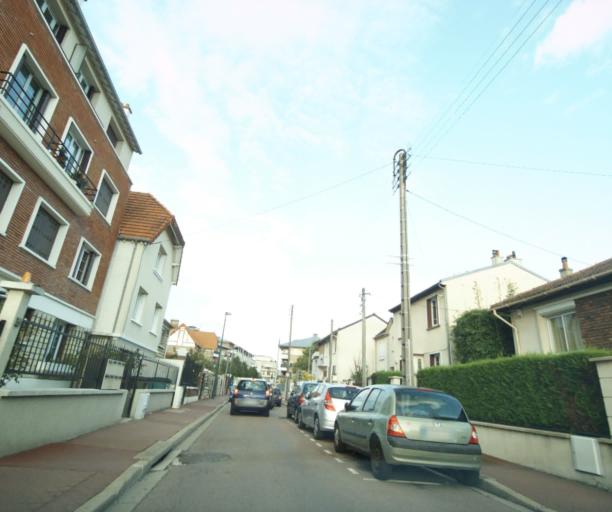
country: FR
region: Ile-de-France
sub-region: Departement de l'Essonne
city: Bievres
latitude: 48.7816
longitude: 2.2377
